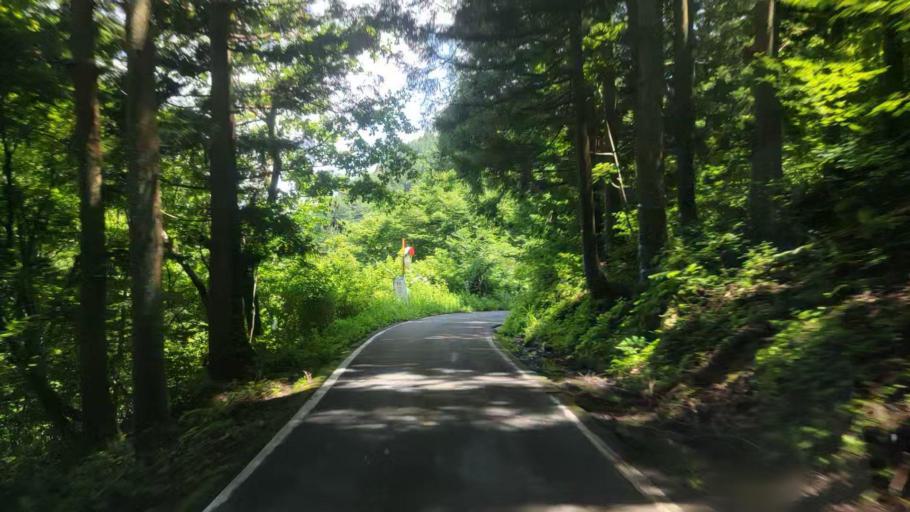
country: JP
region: Fukui
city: Ono
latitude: 35.7622
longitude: 136.5549
